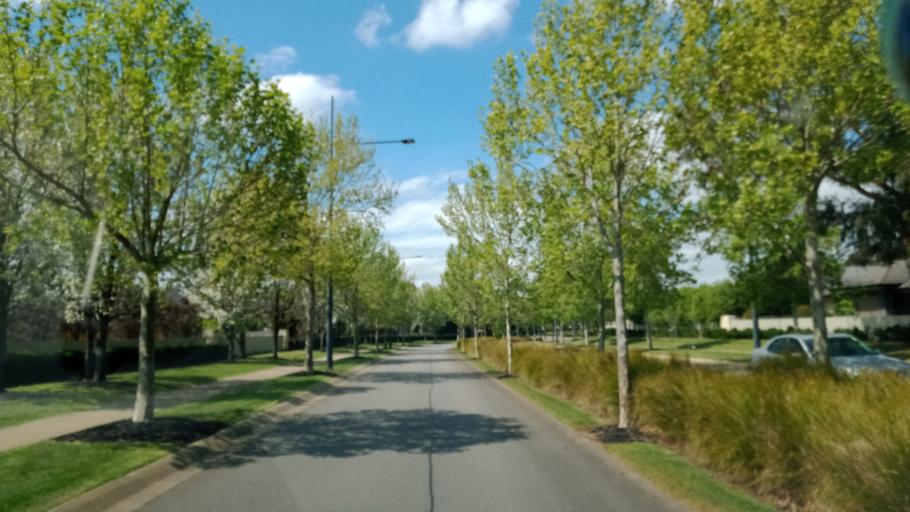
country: AU
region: Victoria
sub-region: Frankston
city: Sandhurst
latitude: -38.0808
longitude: 145.2056
